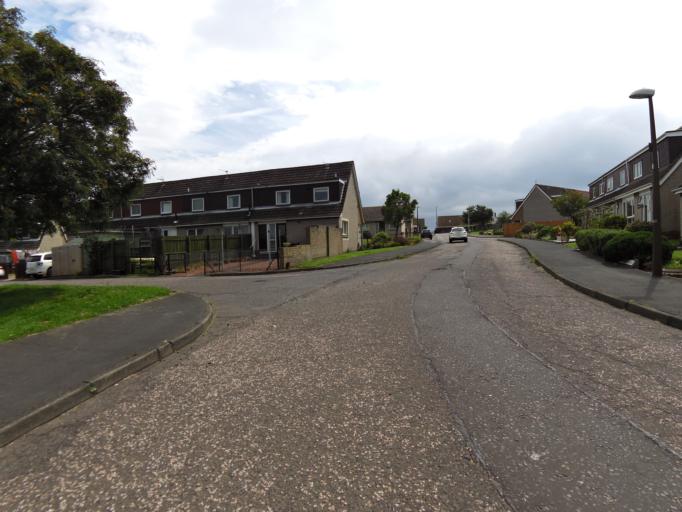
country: GB
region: Scotland
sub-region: East Lothian
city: Musselburgh
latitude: 55.9355
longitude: -3.0678
